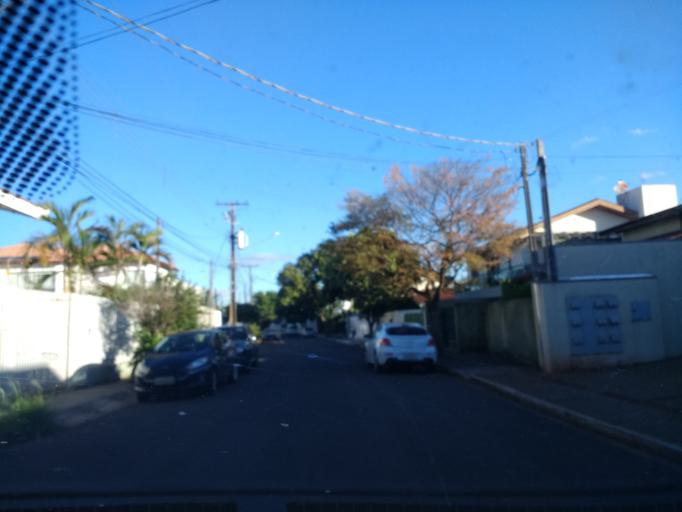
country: BR
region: Parana
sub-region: Londrina
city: Londrina
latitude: -23.3281
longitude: -51.1613
